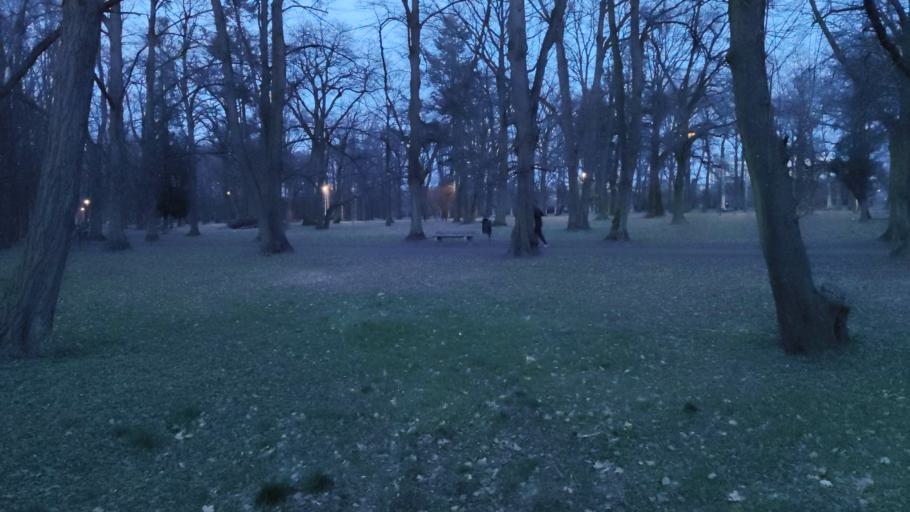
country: PL
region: Lower Silesian Voivodeship
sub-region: Powiat wroclawski
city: Wroclaw
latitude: 51.0778
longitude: 17.0246
